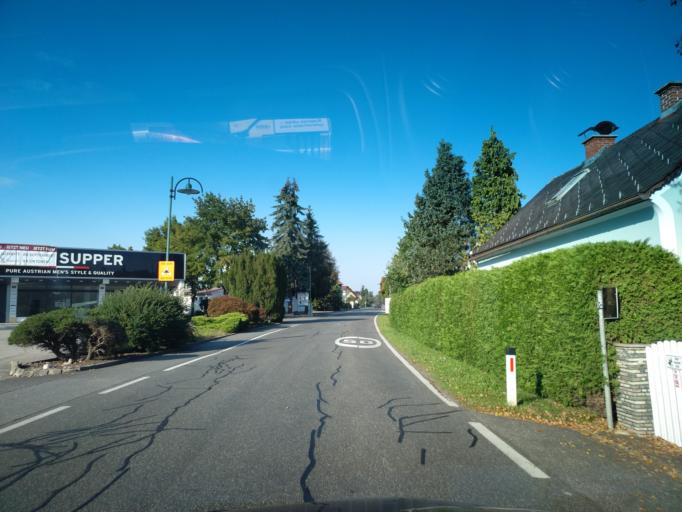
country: AT
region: Styria
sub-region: Politischer Bezirk Leibnitz
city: Kaindorf an der Sulm
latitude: 46.8052
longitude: 15.5432
